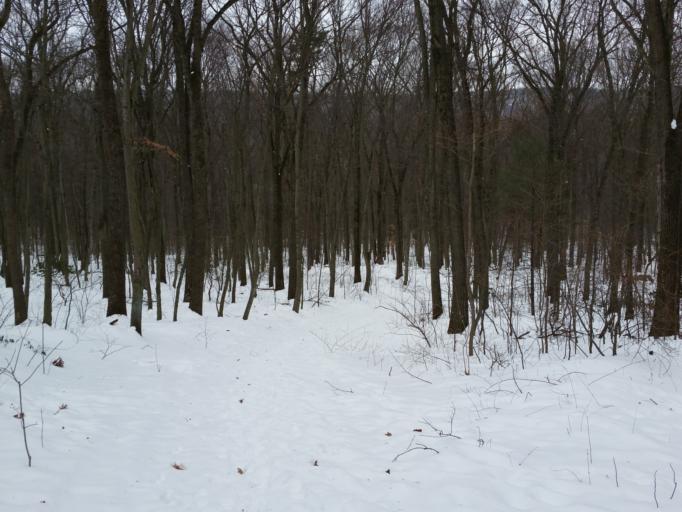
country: US
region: Pennsylvania
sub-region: Dauphin County
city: Lawrence Park
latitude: 40.3592
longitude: -76.8605
